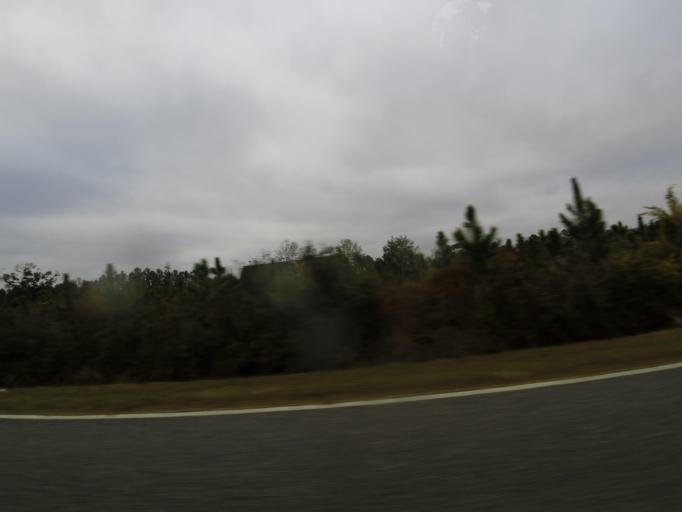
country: US
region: Georgia
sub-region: Charlton County
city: Folkston
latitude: 30.8991
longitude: -82.0709
